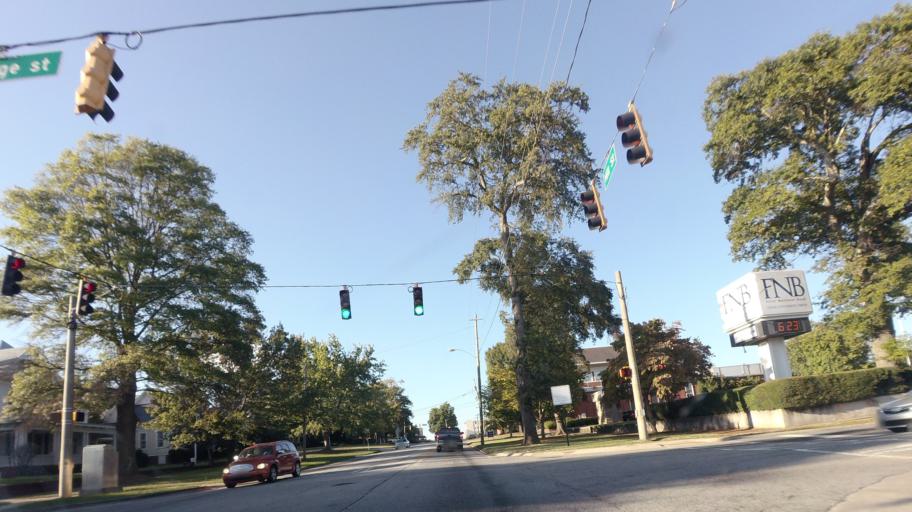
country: US
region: Georgia
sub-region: Spalding County
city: Griffin
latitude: 33.2444
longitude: -84.2639
